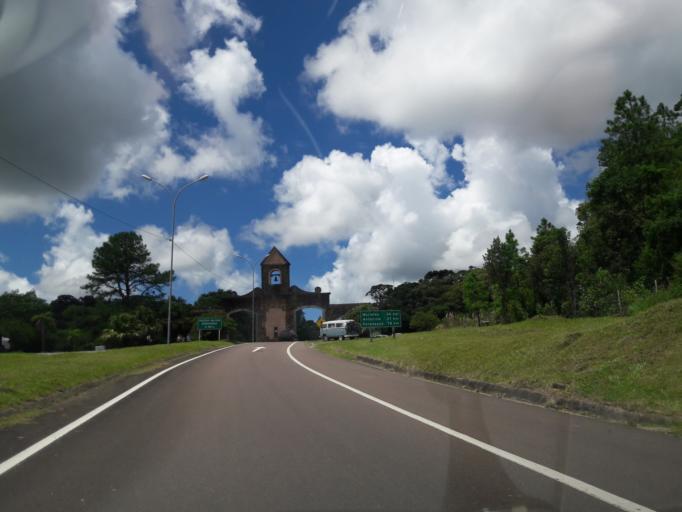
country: BR
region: Parana
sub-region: Campina Grande Do Sul
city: Campina Grande do Sul
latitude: -25.3057
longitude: -48.9458
